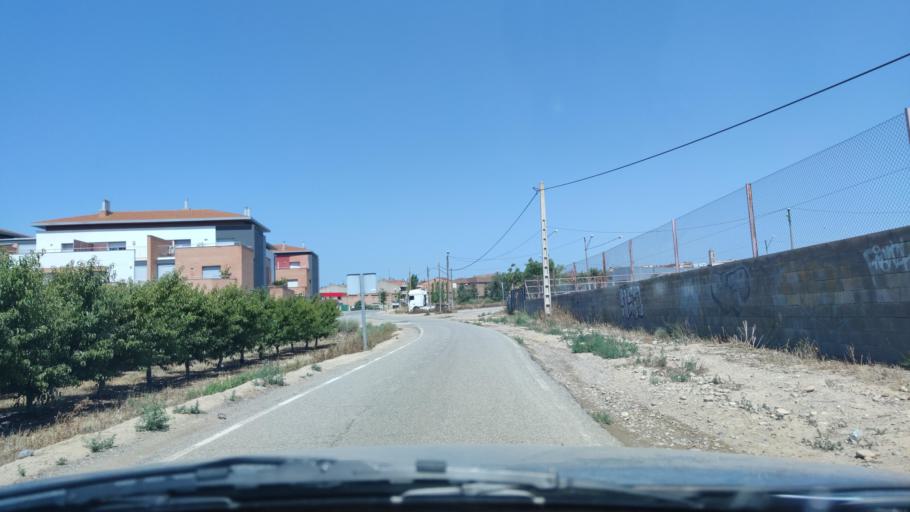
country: ES
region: Catalonia
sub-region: Provincia de Lleida
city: Alpicat
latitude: 41.6615
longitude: 0.5595
